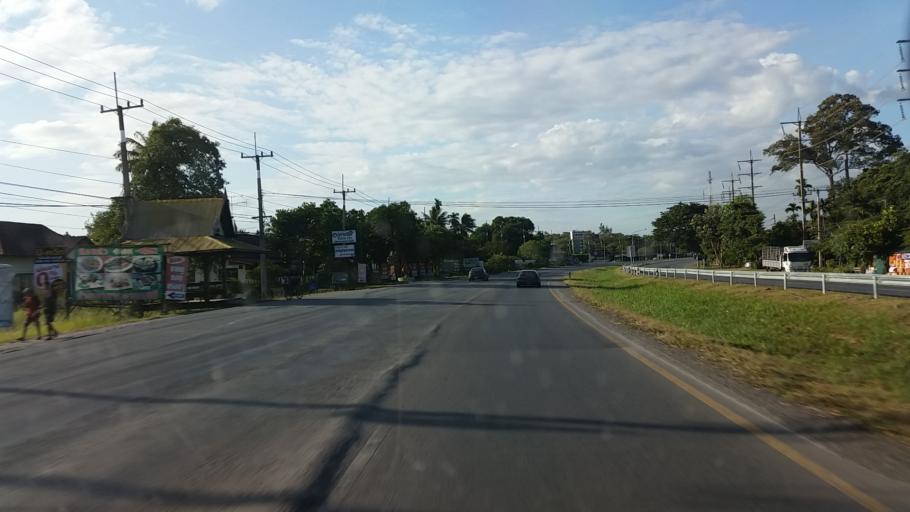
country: TH
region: Sara Buri
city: Chaloem Phra Kiat
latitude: 14.6706
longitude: 100.8933
